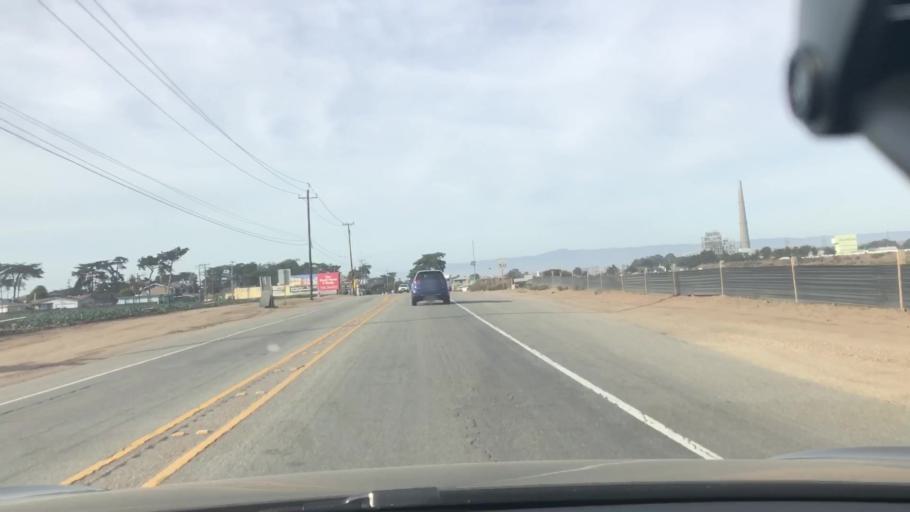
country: US
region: California
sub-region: Monterey County
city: Castroville
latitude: 36.7894
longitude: -121.7829
